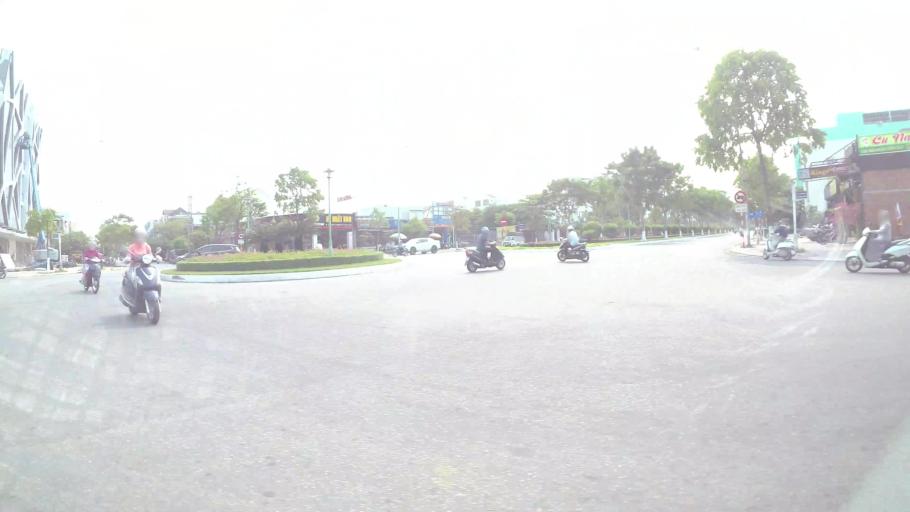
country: VN
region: Da Nang
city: Son Tra
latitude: 16.0406
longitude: 108.2178
